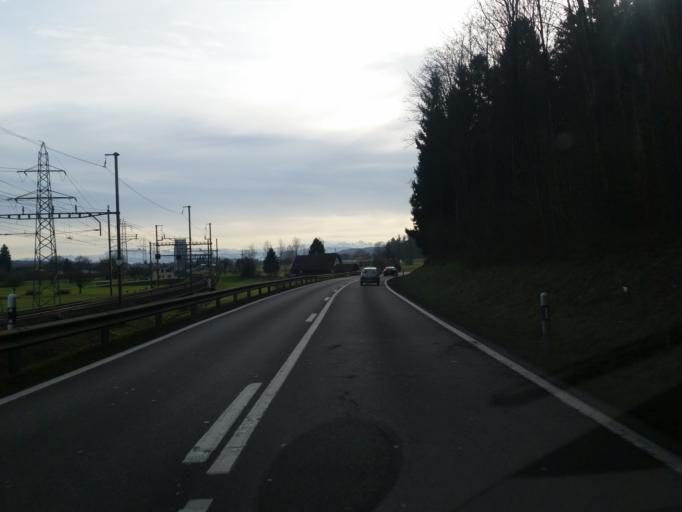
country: CH
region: Aargau
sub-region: Bezirk Lenzburg
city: Othmarsingen
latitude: 47.3859
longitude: 8.2113
